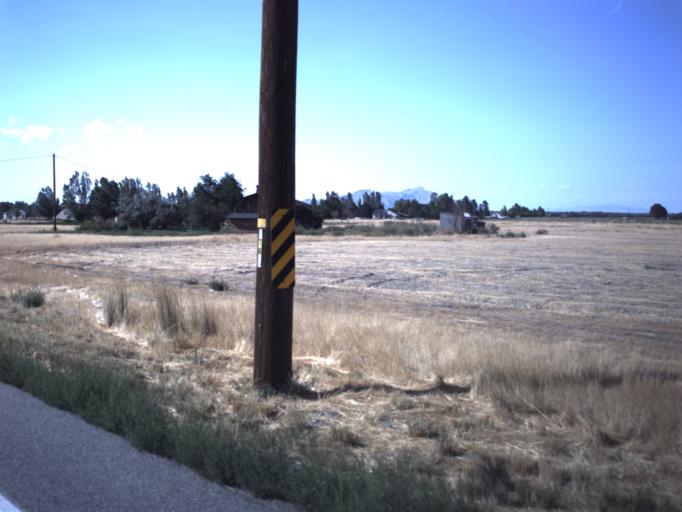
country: US
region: Utah
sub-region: Tooele County
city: Grantsville
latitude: 40.5903
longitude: -112.4192
